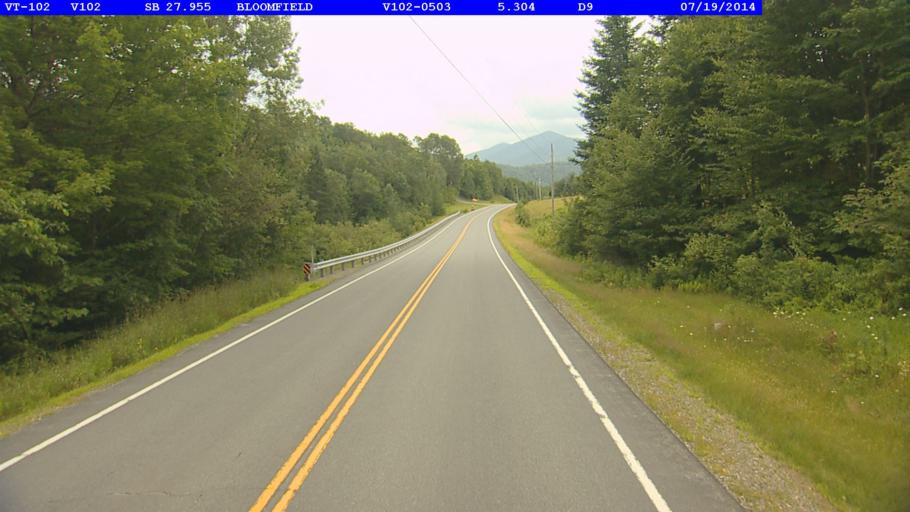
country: US
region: New Hampshire
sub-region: Coos County
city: Colebrook
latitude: 44.8069
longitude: -71.5740
